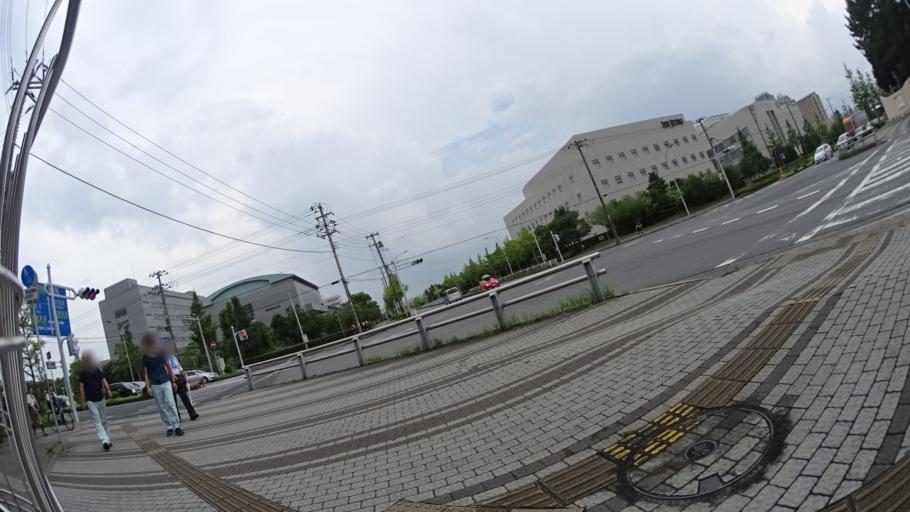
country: JP
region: Chiba
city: Funabashi
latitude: 35.6504
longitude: 140.0476
